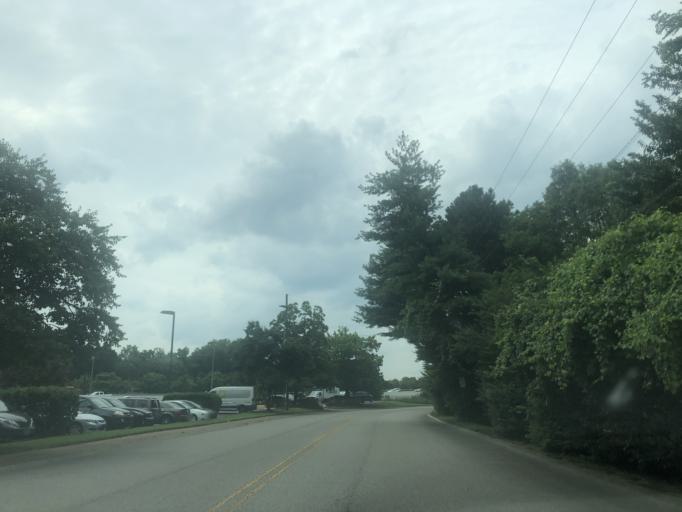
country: US
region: Tennessee
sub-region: Davidson County
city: Nashville
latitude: 36.1553
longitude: -86.6906
